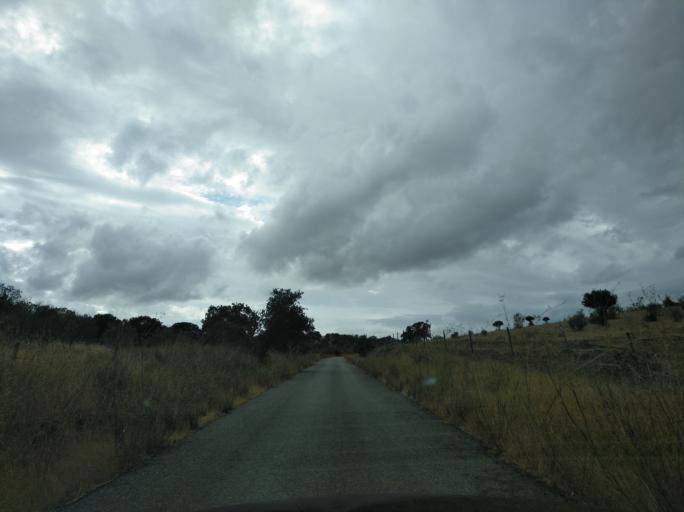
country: PT
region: Portalegre
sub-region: Campo Maior
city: Campo Maior
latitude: 39.0363
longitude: -7.1374
